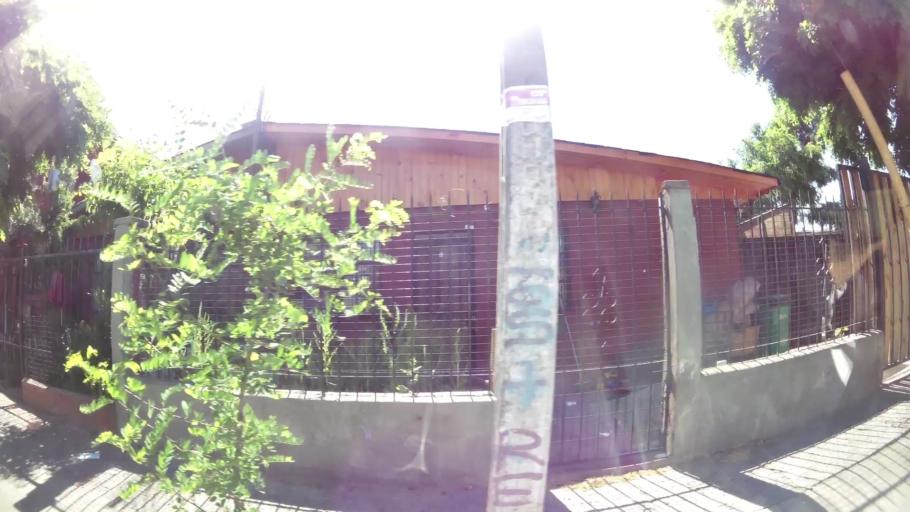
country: CL
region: Santiago Metropolitan
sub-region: Provincia de Maipo
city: San Bernardo
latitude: -33.5808
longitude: -70.6903
